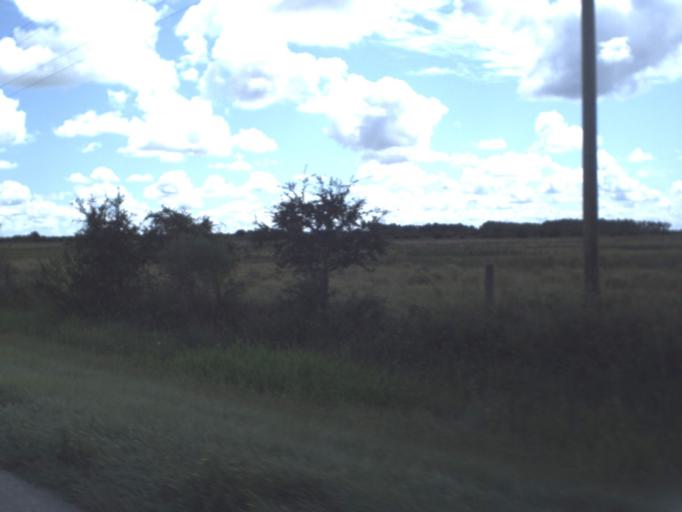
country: US
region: Florida
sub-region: Highlands County
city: Placid Lakes
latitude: 27.2088
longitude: -81.4195
